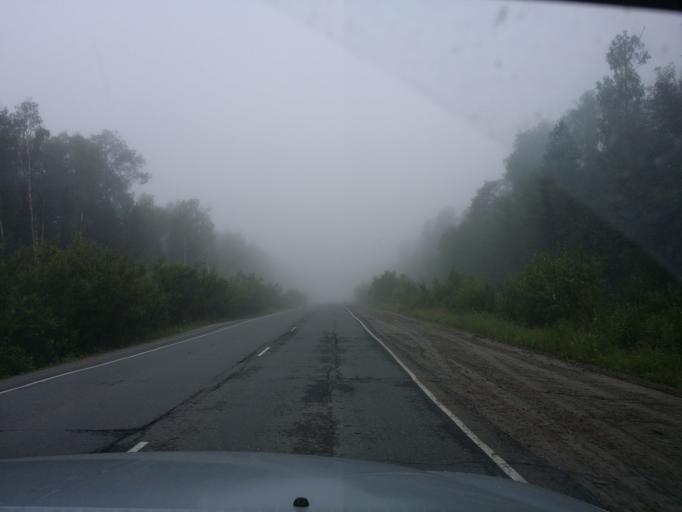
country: RU
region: Khanty-Mansiyskiy Avtonomnyy Okrug
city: Gornopravdinsk
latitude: 59.6381
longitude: 69.8377
